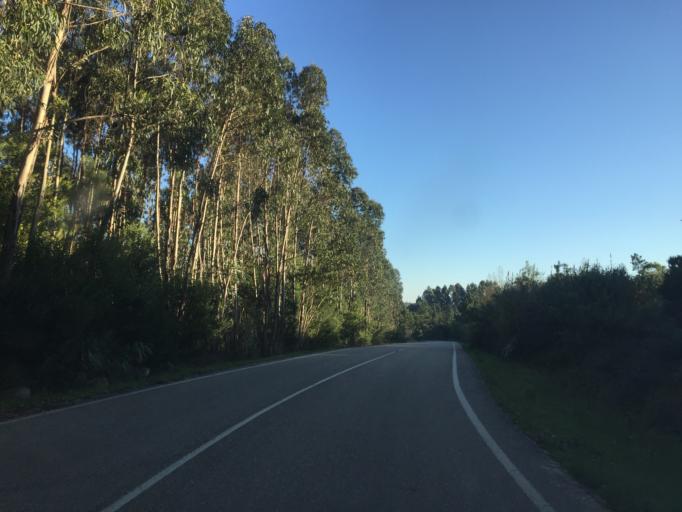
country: PT
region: Coimbra
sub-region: Figueira da Foz
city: Alhadas
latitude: 40.1572
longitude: -8.7995
